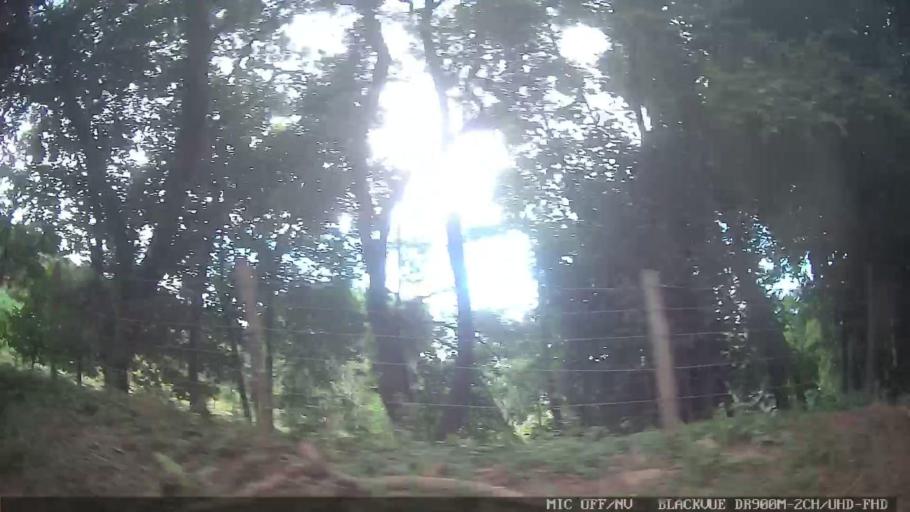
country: BR
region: Sao Paulo
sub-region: Bom Jesus Dos Perdoes
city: Bom Jesus dos Perdoes
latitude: -23.1245
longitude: -46.4988
